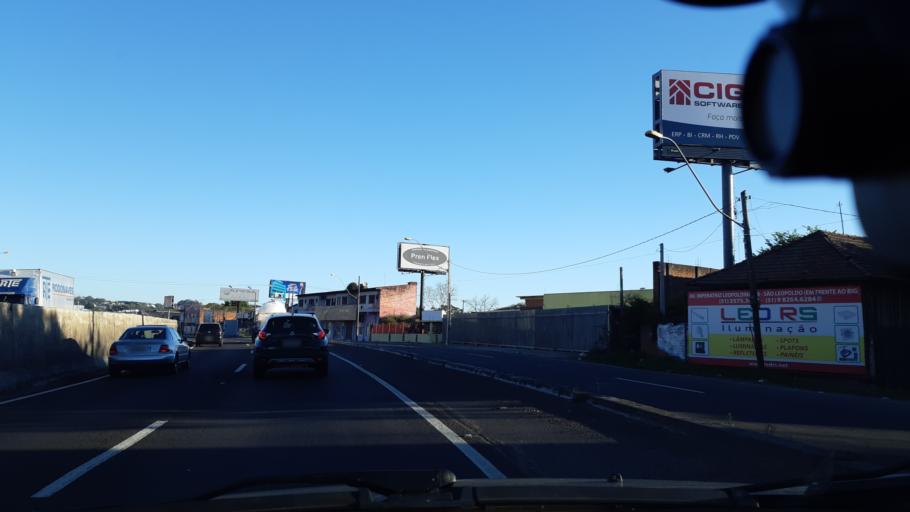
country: BR
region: Rio Grande do Sul
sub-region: Sao Leopoldo
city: Sao Leopoldo
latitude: -29.7648
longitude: -51.1540
